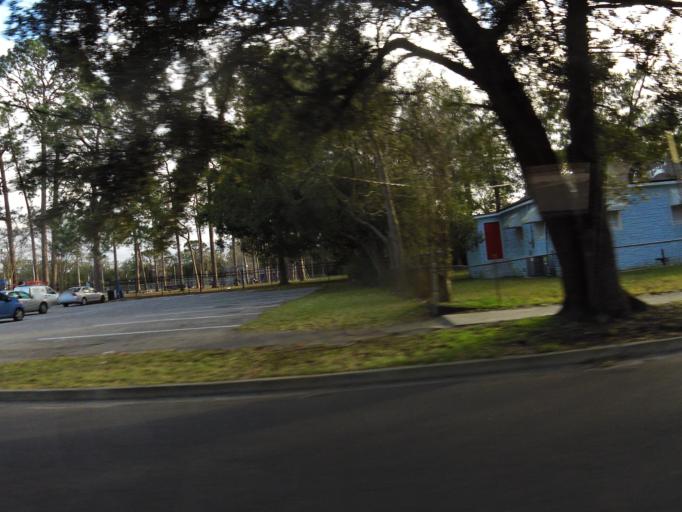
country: US
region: Florida
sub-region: Duval County
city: Jacksonville
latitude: 30.3066
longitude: -81.7195
